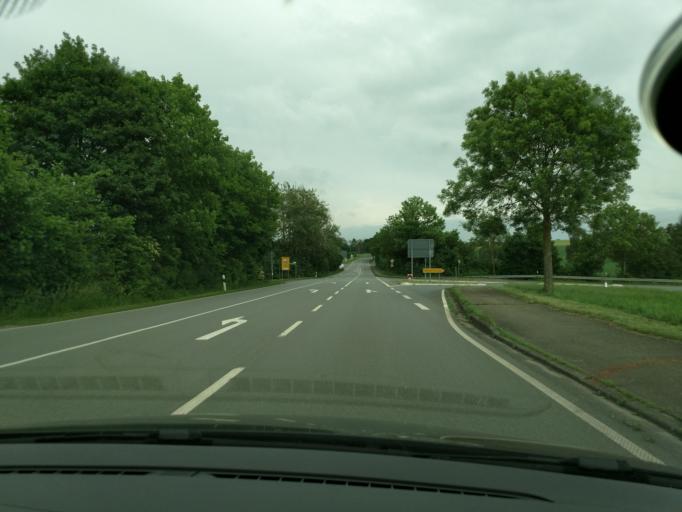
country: DE
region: Hesse
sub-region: Regierungsbezirk Kassel
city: Bad Arolsen
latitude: 51.3569
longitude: 8.9928
